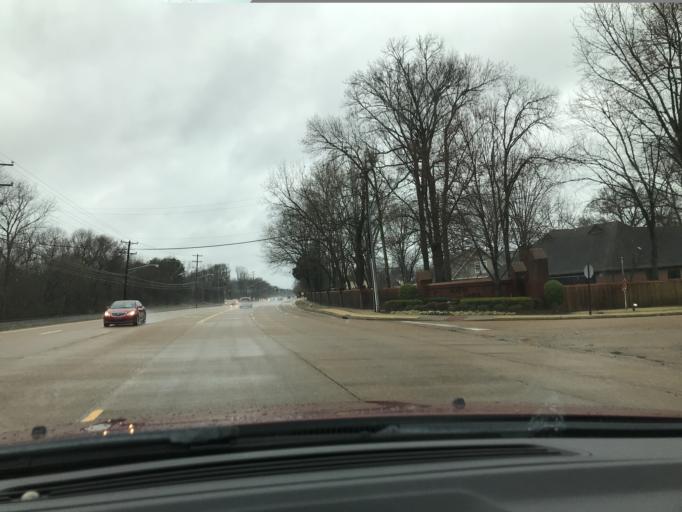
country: US
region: Tennessee
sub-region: Shelby County
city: Collierville
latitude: 35.0482
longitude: -89.7204
